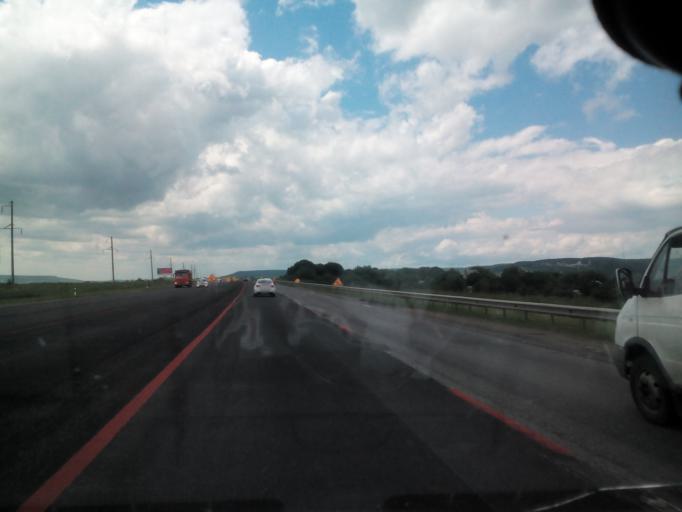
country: RU
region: Stavropol'skiy
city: Tatarka
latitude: 44.9532
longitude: 41.9723
